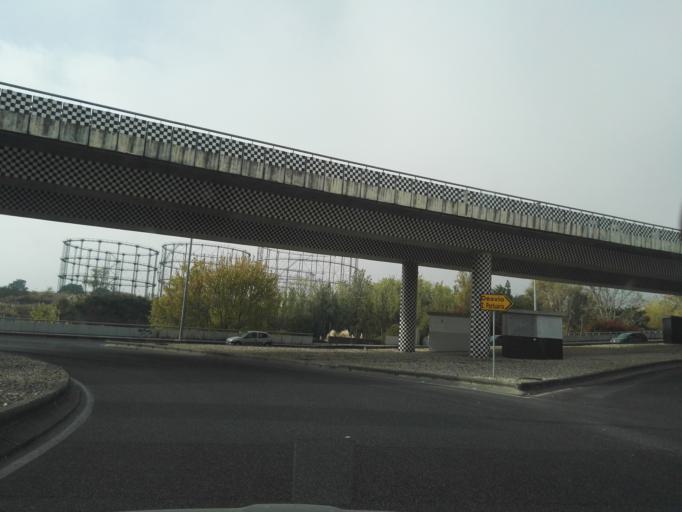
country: PT
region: Lisbon
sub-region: Loures
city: Moscavide
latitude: 38.7544
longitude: -9.0971
